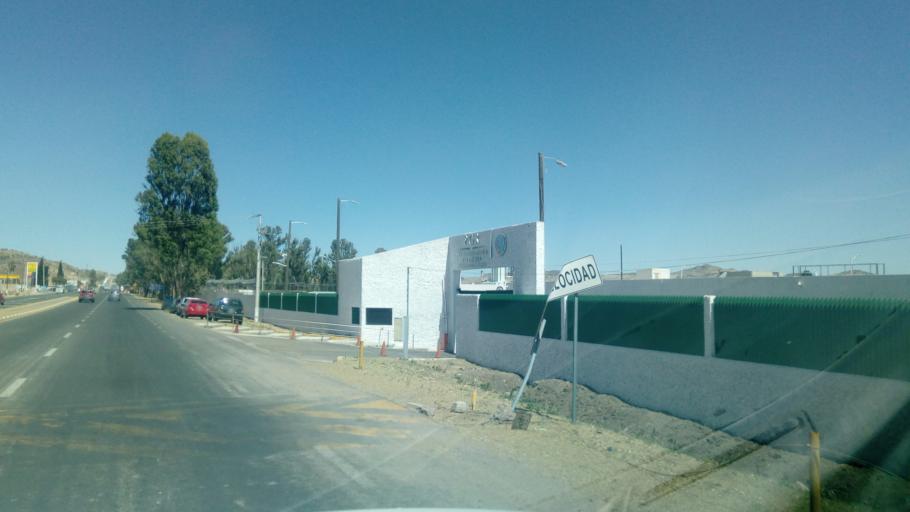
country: MX
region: Durango
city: Victoria de Durango
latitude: 24.0753
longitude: -104.6622
